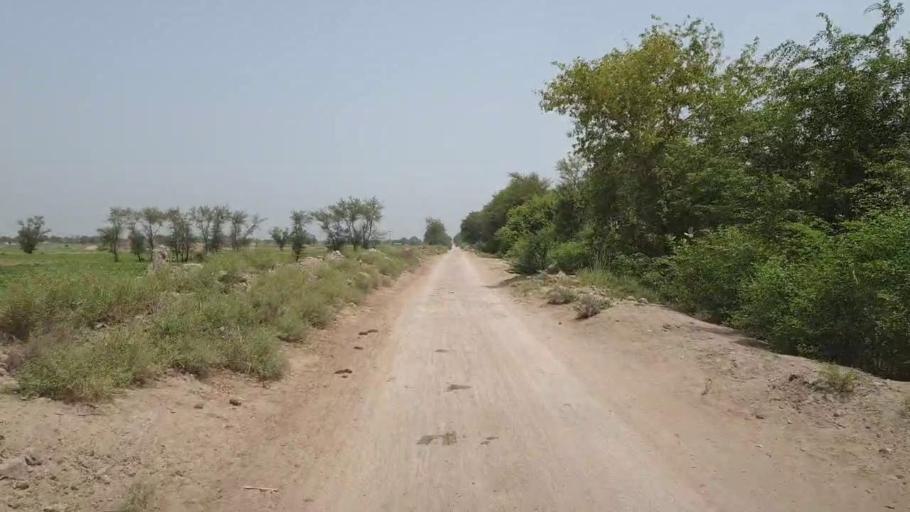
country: PK
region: Sindh
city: Nawabshah
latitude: 26.3082
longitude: 68.3024
